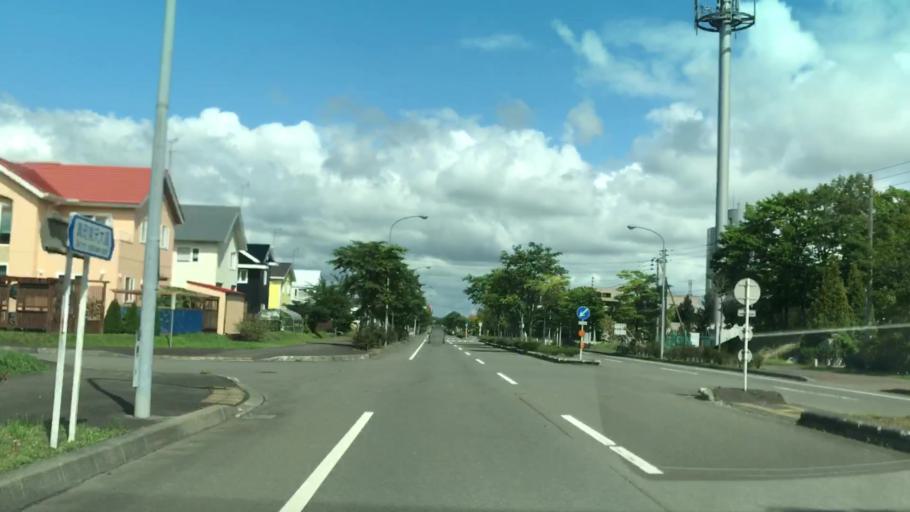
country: JP
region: Hokkaido
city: Chitose
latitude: 42.7778
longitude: 141.5998
